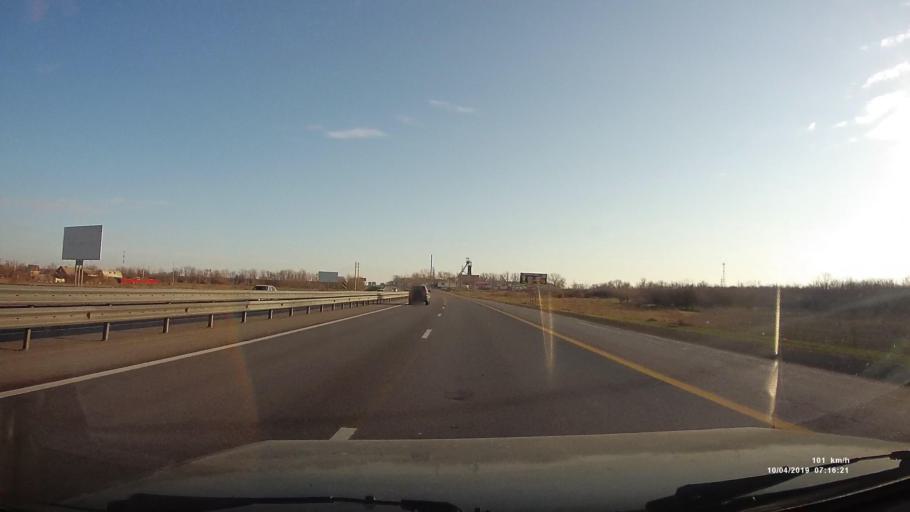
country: RU
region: Rostov
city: Ayutinskiy
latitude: 47.7676
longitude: 40.1558
